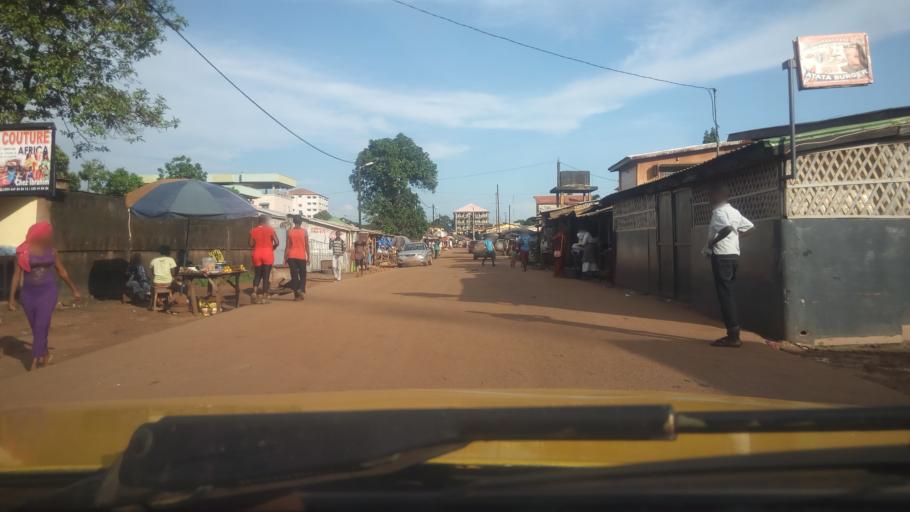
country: GN
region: Conakry
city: Conakry
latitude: 9.6208
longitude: -13.6087
